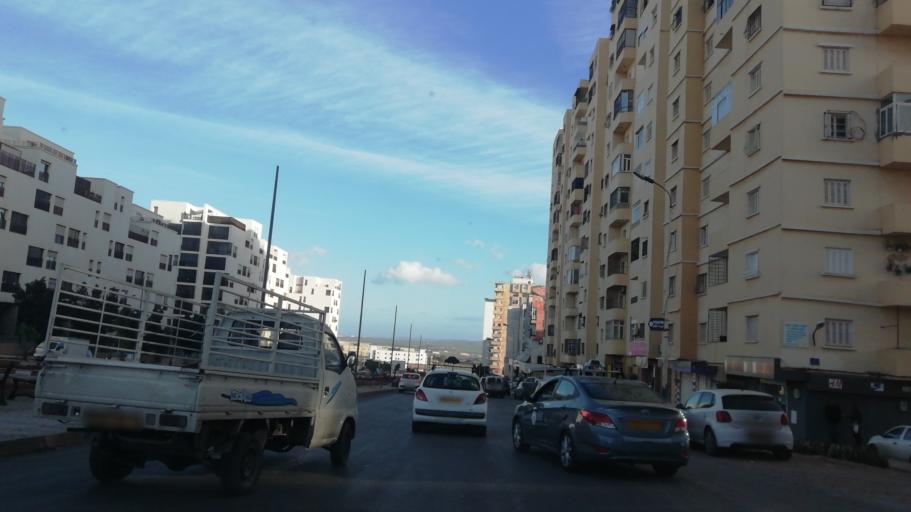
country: DZ
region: Oran
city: Bir el Djir
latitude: 35.7062
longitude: -0.5581
